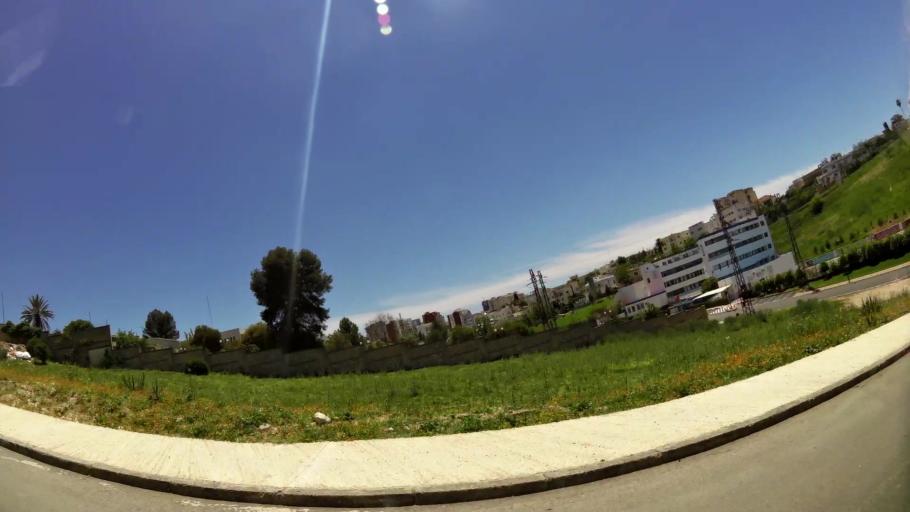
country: MA
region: Meknes-Tafilalet
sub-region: Meknes
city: Meknes
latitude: 33.9065
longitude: -5.5493
